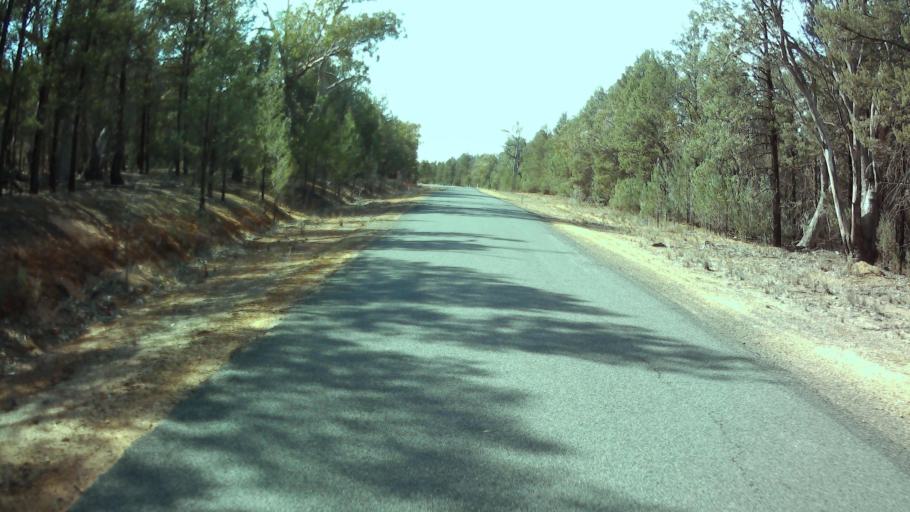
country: AU
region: New South Wales
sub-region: Weddin
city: Grenfell
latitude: -33.7354
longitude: 148.0405
